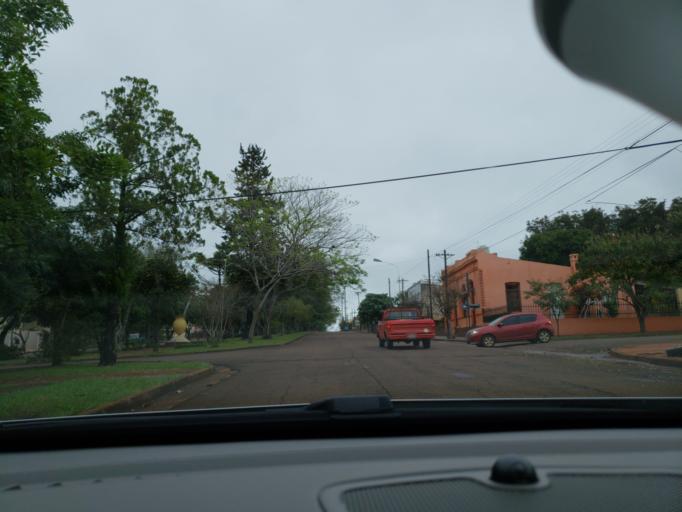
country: AR
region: Misiones
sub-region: Departamento de Apostoles
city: Apostoles
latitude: -27.9084
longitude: -55.7486
